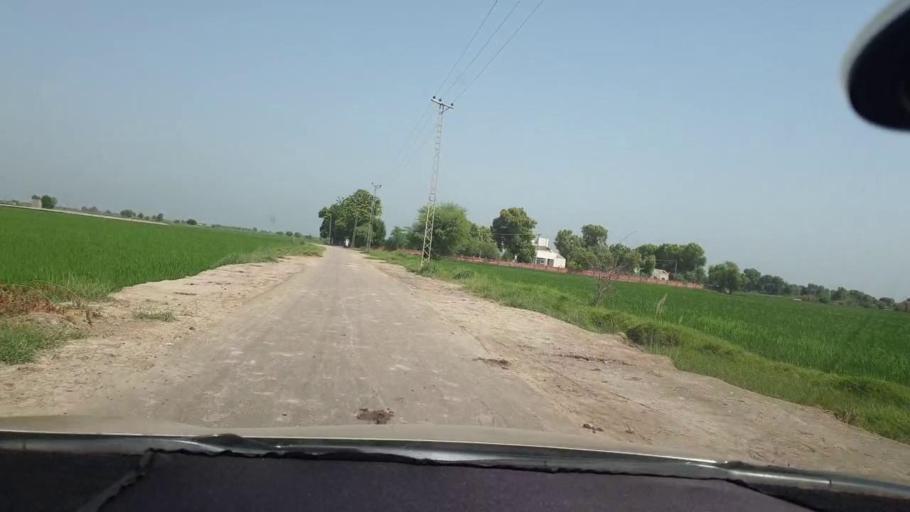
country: PK
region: Sindh
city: Goth Garelo
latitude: 27.4982
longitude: 68.0204
